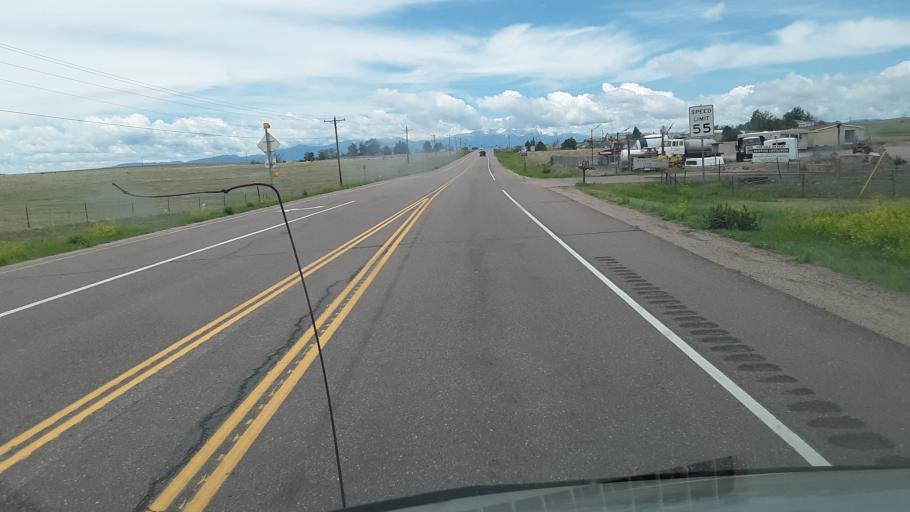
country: US
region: Colorado
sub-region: El Paso County
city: Ellicott
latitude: 38.8387
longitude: -104.5362
